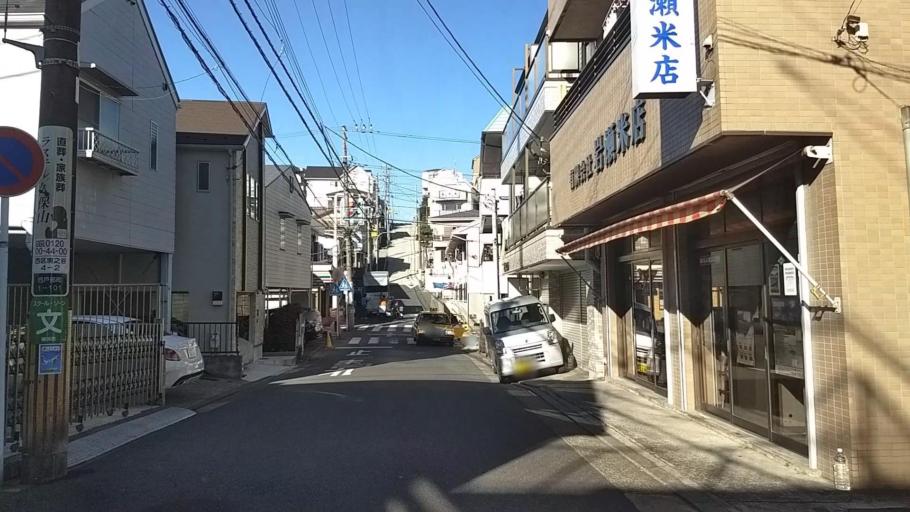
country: JP
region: Kanagawa
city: Yokohama
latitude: 35.4477
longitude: 139.6212
